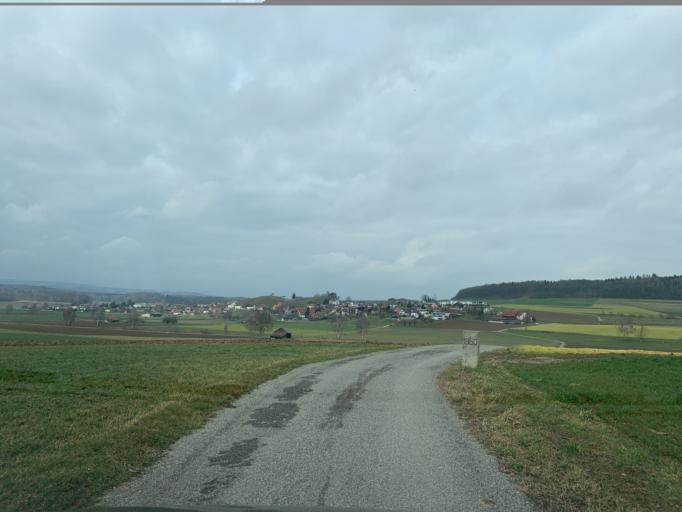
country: CH
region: Thurgau
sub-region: Frauenfeld District
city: Diessenhofen
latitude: 47.6964
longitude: 8.7265
